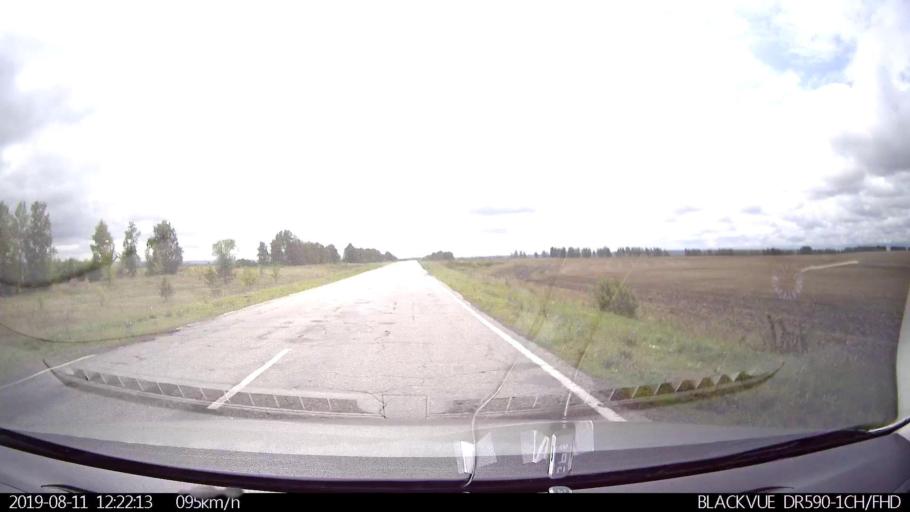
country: RU
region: Ulyanovsk
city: Ignatovka
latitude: 53.9107
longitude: 47.9549
